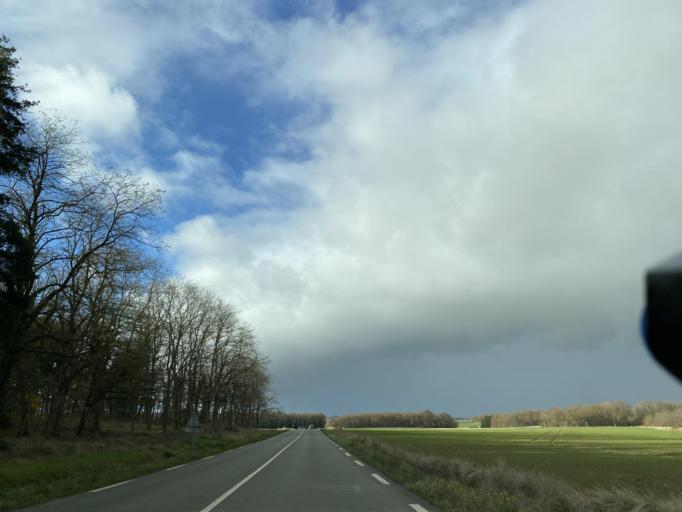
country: FR
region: Centre
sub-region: Departement d'Eure-et-Loir
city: Mainvilliers
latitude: 48.4643
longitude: 1.4273
